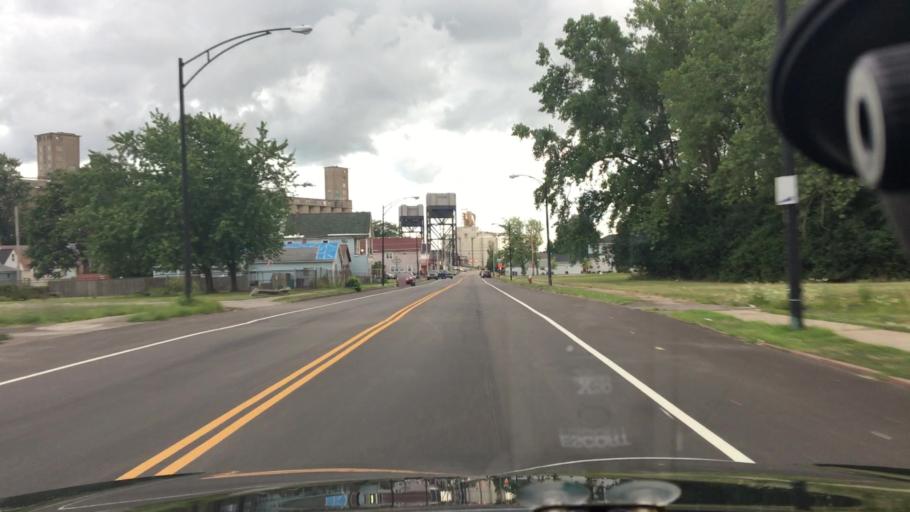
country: US
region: New York
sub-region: Erie County
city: Buffalo
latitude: 42.8668
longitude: -78.8662
